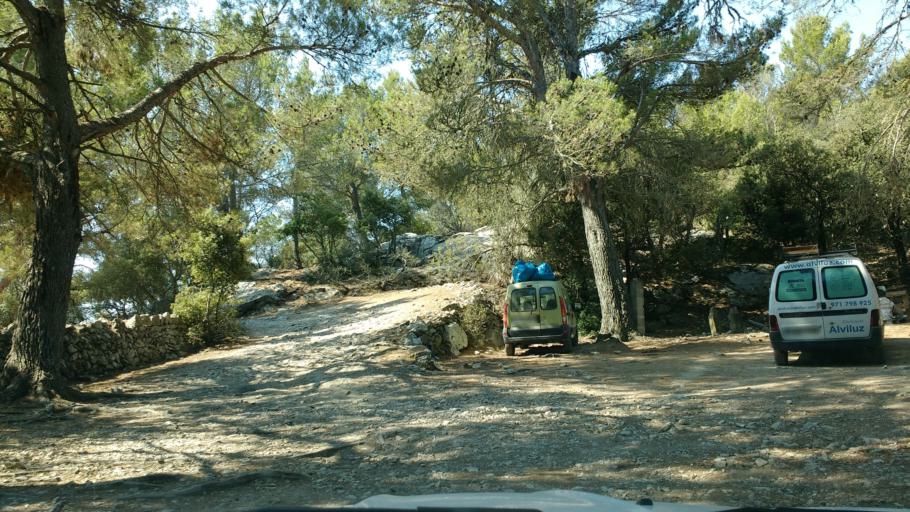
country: ES
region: Balearic Islands
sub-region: Illes Balears
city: Alaro
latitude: 39.7351
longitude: 2.7868
